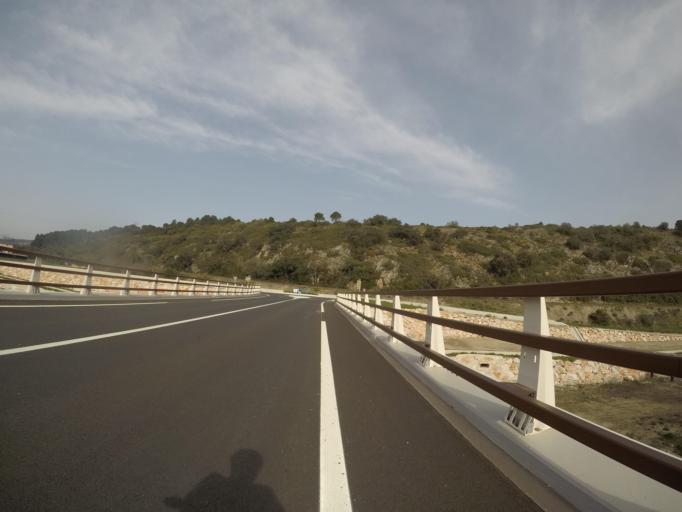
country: FR
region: Languedoc-Roussillon
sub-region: Departement des Pyrenees-Orientales
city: Estagel
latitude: 42.7765
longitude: 2.7084
